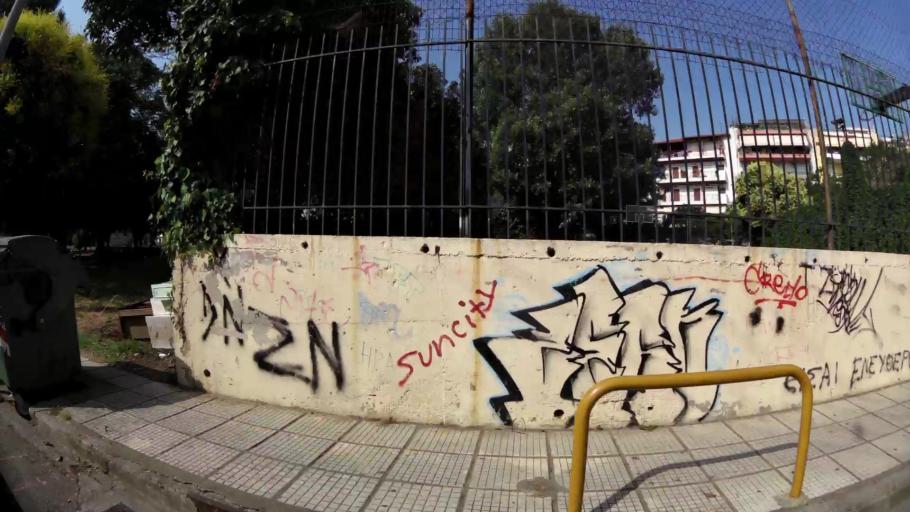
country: GR
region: Central Macedonia
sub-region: Nomos Thessalonikis
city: Stavroupoli
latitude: 40.6709
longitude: 22.9290
